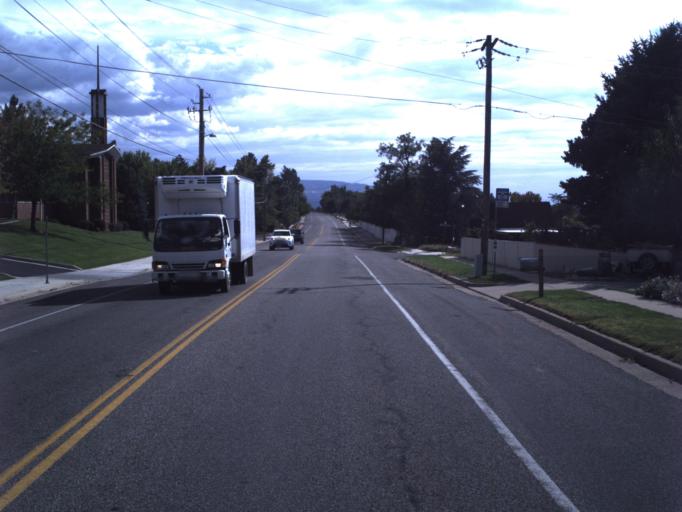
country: US
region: Utah
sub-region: Davis County
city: Farmington
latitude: 40.9696
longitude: -111.8834
